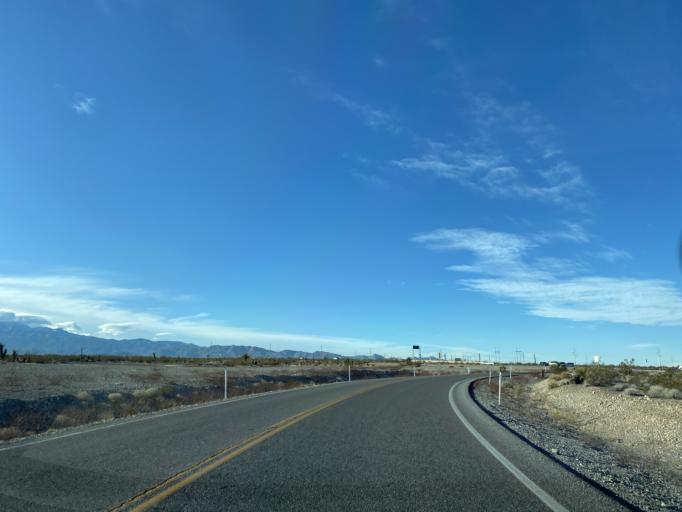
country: US
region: Nevada
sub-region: Clark County
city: Summerlin South
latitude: 36.3250
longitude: -115.3153
